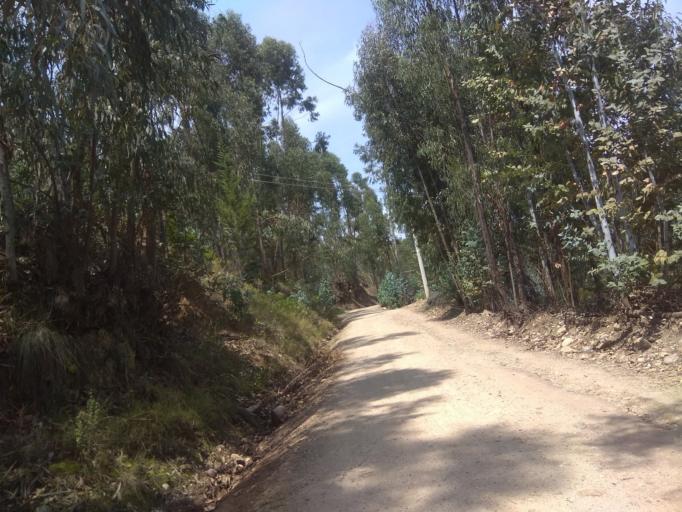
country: CO
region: Boyaca
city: Socha Viejo
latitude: 5.9788
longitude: -72.7263
